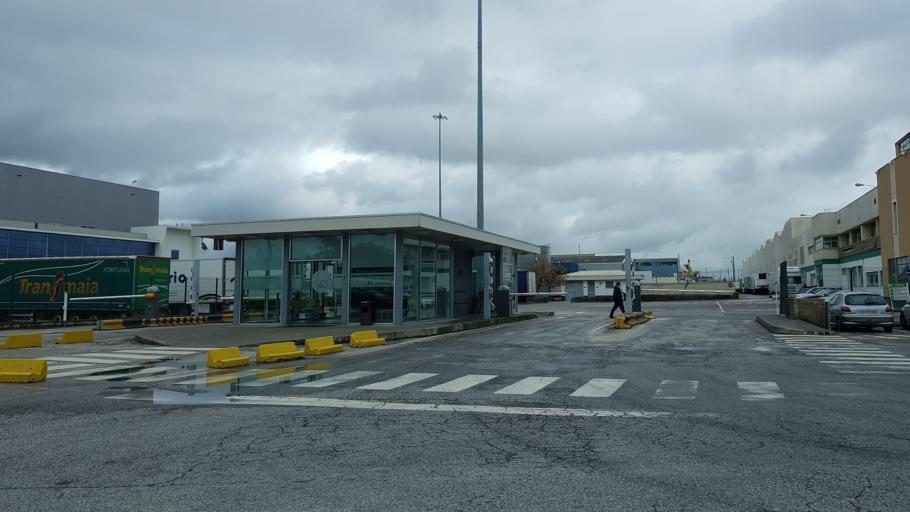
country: PT
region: Lisbon
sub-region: Alenquer
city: Carregado
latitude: 39.0309
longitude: -8.9670
